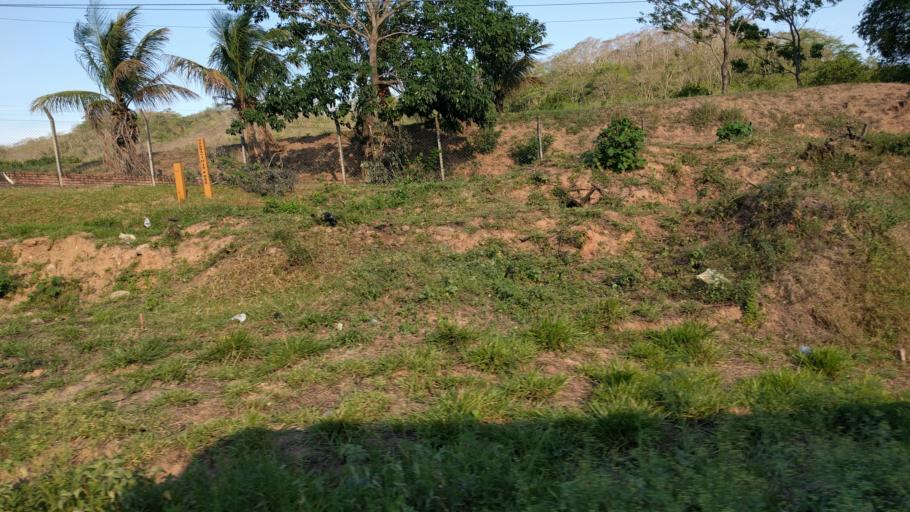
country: BO
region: Santa Cruz
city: Jorochito
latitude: -18.0815
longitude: -63.4489
